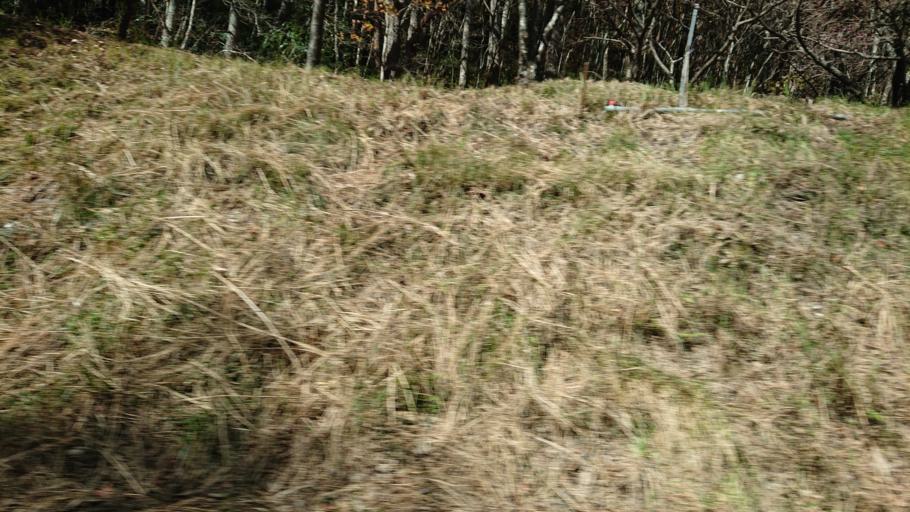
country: TW
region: Taiwan
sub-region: Hualien
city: Hualian
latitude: 24.3489
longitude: 121.3078
